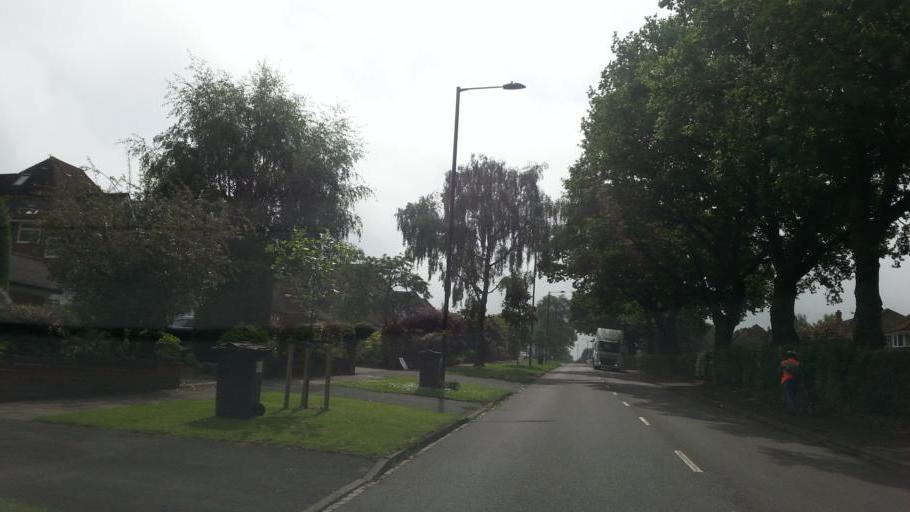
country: GB
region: England
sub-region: Walsall
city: Streetly
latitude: 52.5918
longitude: -1.8511
